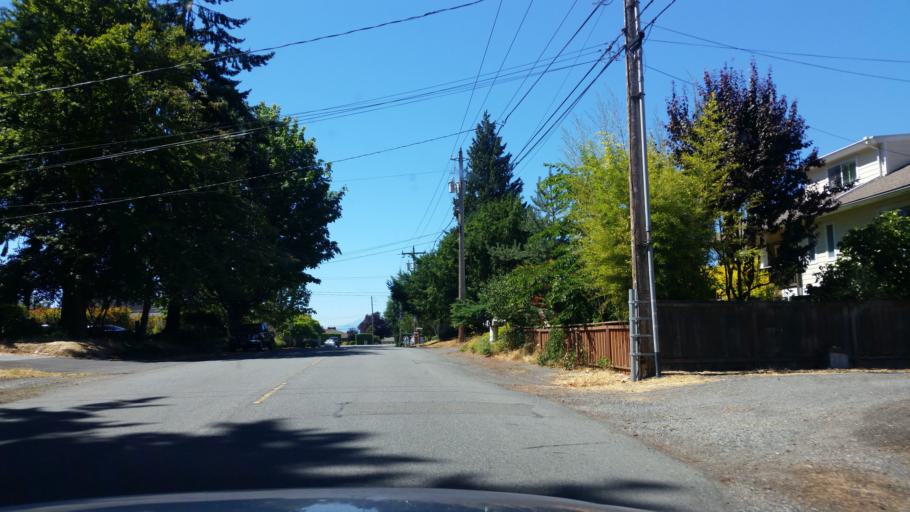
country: US
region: Washington
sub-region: King County
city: Shoreline
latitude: 47.7633
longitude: -122.3641
